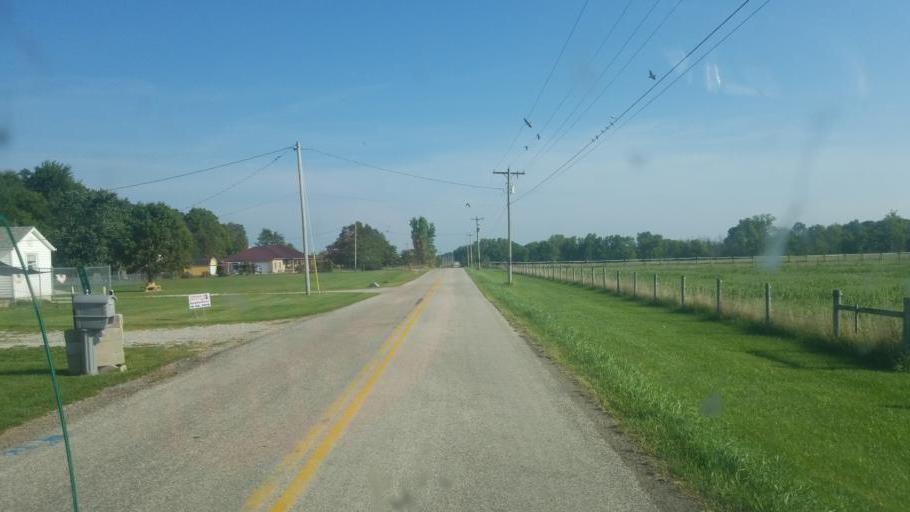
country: US
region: Ohio
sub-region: Huron County
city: New London
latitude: 41.0196
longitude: -82.3539
